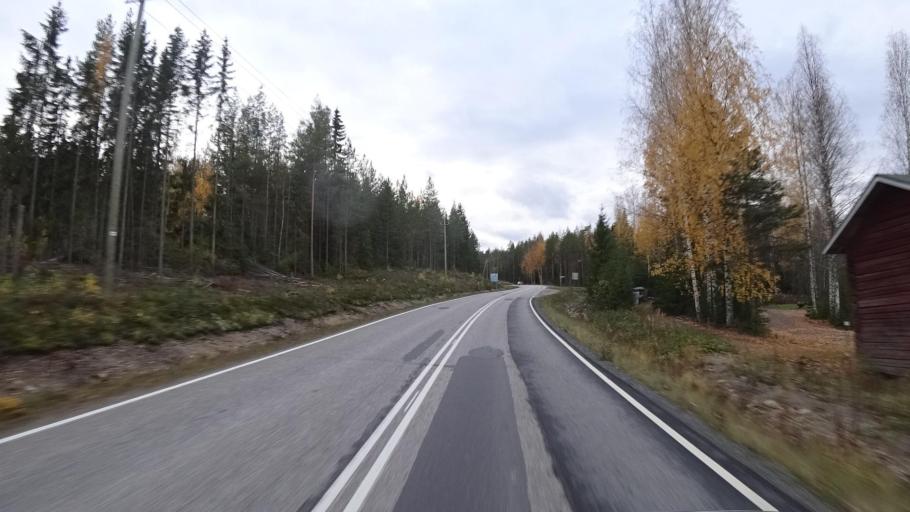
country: FI
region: Central Finland
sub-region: Joutsa
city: Joutsa
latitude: 61.7934
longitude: 26.1719
